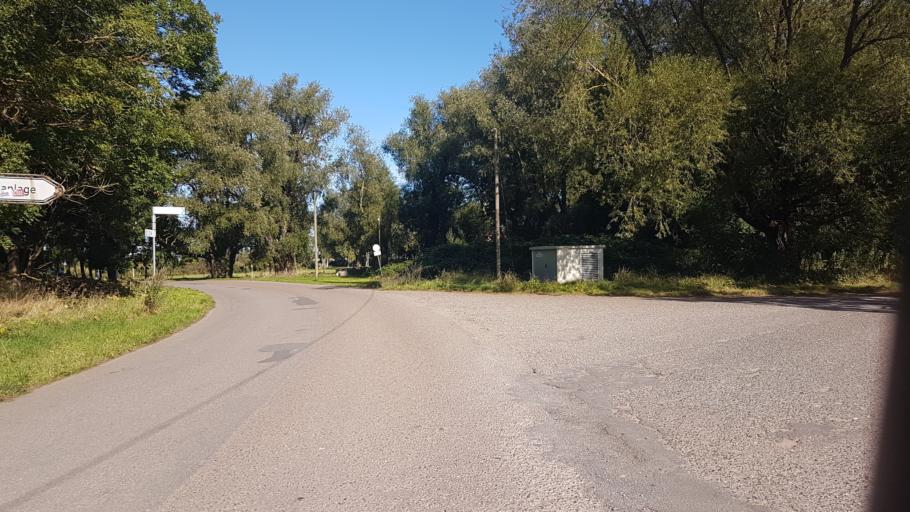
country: DE
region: Mecklenburg-Vorpommern
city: Sagard
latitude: 54.5186
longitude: 13.5306
